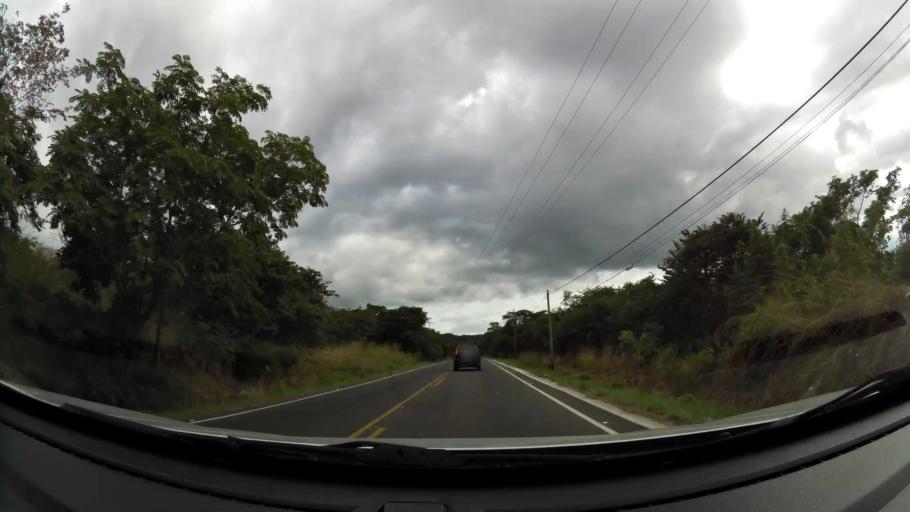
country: CR
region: Guanacaste
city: Nandayure
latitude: 10.2473
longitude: -85.2260
